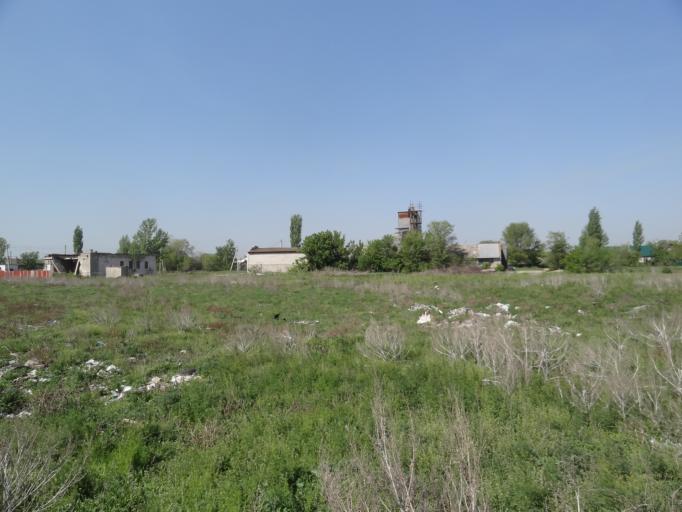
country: RU
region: Saratov
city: Privolzhskiy
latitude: 51.4146
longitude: 46.1026
